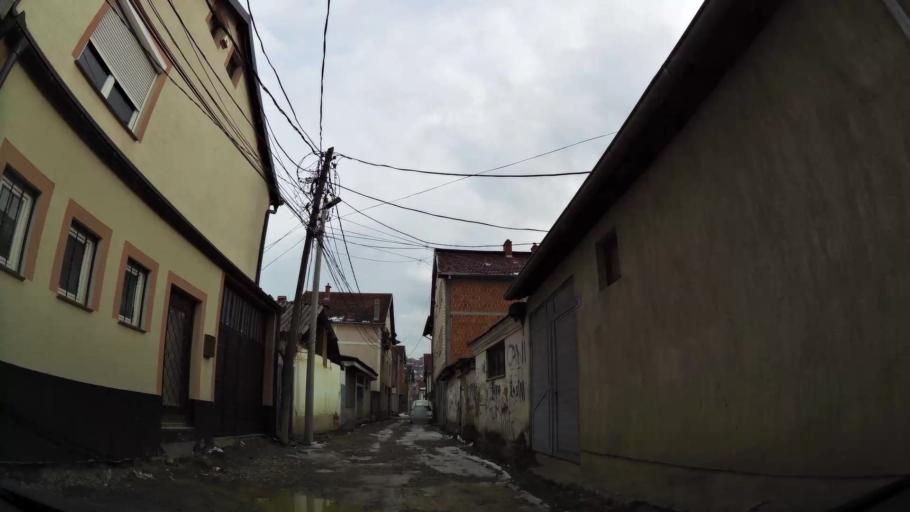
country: XK
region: Pristina
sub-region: Komuna e Prishtines
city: Pristina
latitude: 42.6741
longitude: 21.1694
